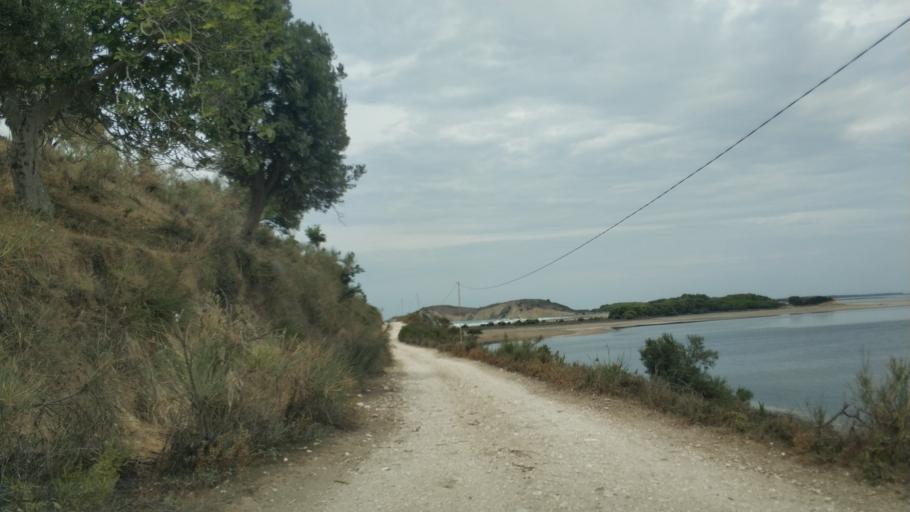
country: AL
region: Vlore
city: Vlore
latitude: 40.5181
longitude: 19.3924
